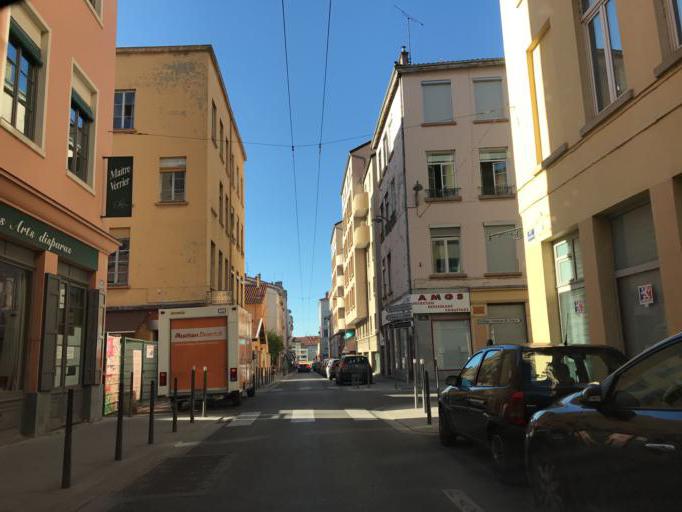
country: FR
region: Rhone-Alpes
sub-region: Departement du Rhone
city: Caluire-et-Cuire
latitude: 45.7781
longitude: 4.8348
